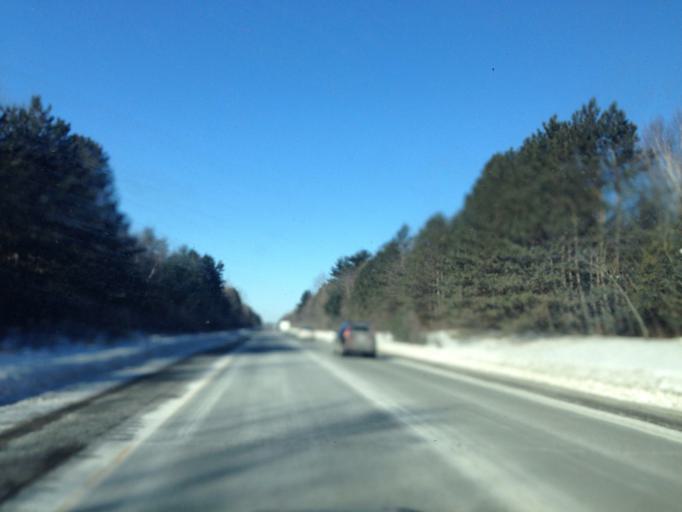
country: CA
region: Ontario
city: Ottawa
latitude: 45.3635
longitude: -75.4923
